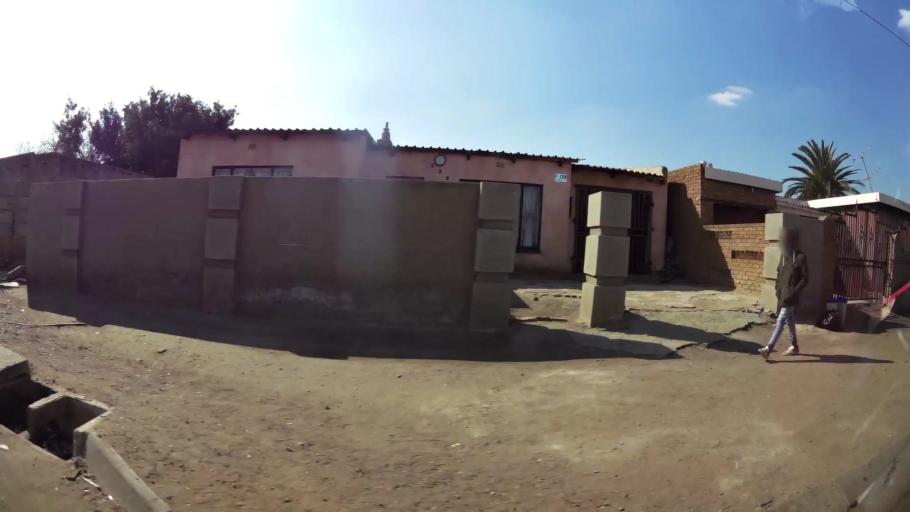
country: ZA
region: Gauteng
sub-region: Ekurhuleni Metropolitan Municipality
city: Brakpan
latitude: -26.1520
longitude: 28.4080
